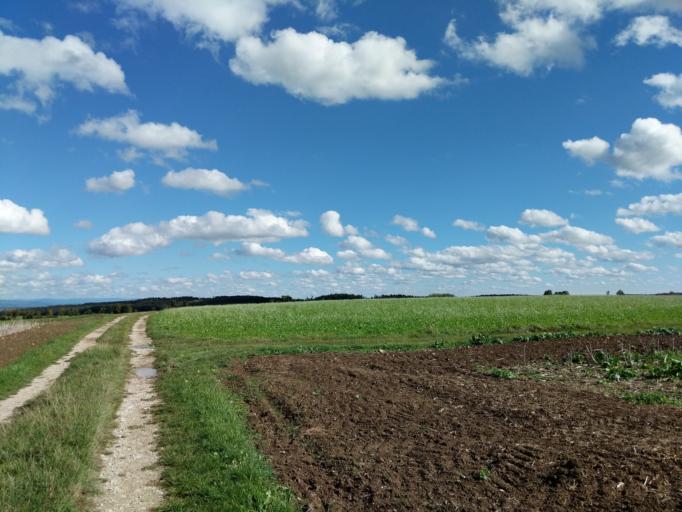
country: DE
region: Bavaria
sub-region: Lower Bavaria
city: Bad Abbach
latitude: 48.9497
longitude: 12.0517
